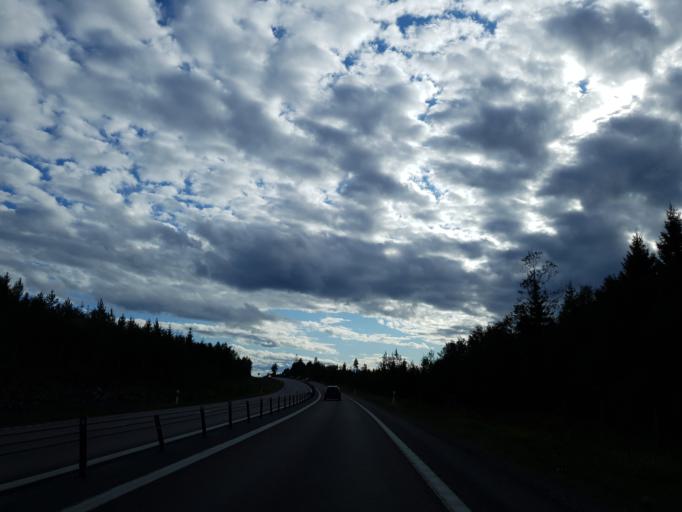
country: SE
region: Vaesternorrland
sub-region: Haernoesands Kommun
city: Haernoesand
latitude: 62.6064
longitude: 17.8213
